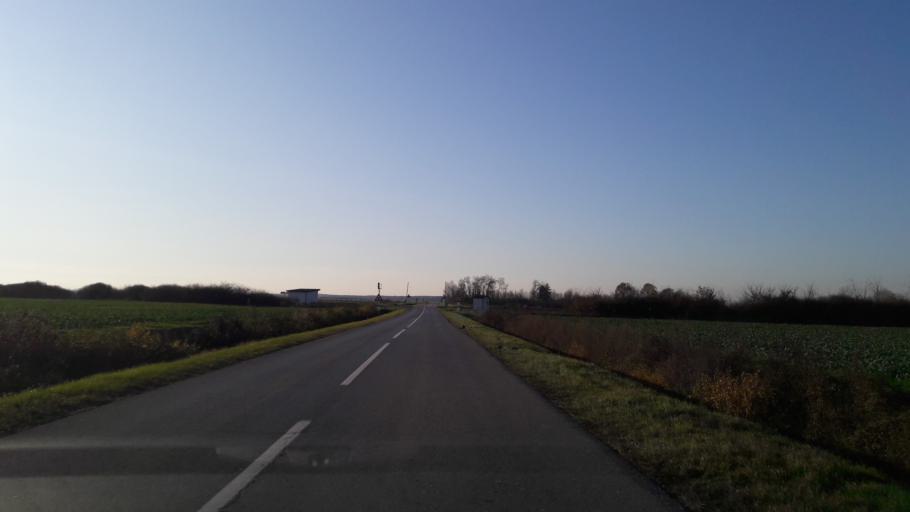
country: HR
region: Osjecko-Baranjska
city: Vuka
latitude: 45.4217
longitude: 18.5261
